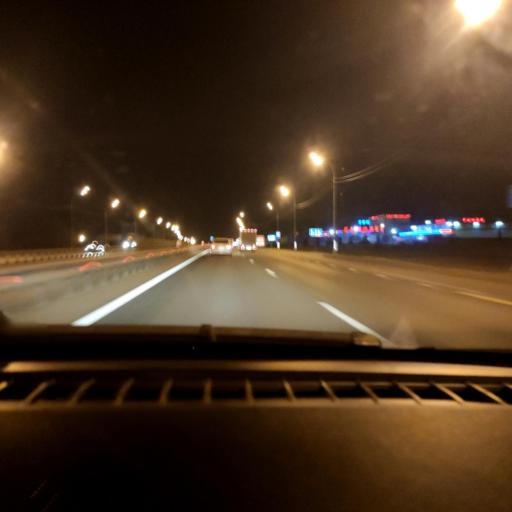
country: RU
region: Lipetsk
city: Khlevnoye
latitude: 52.1107
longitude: 39.1842
